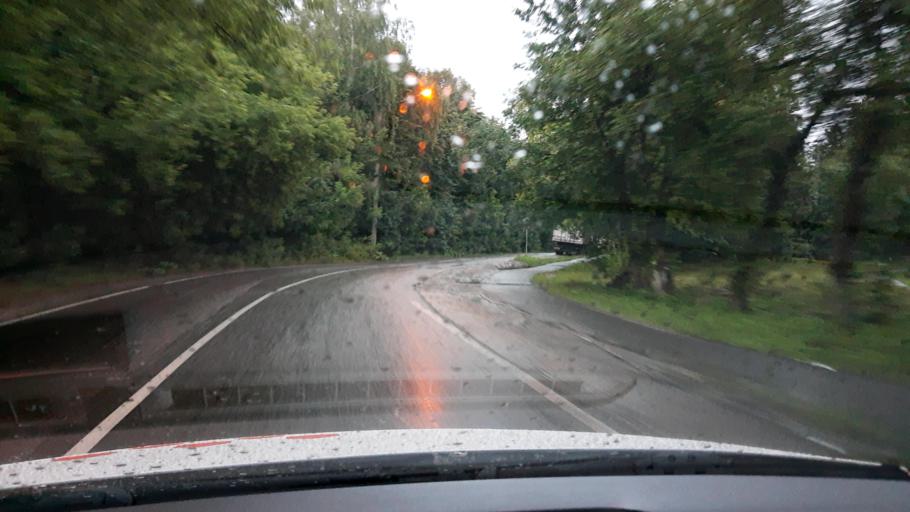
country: RU
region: Moskovskaya
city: Biryulevo Zapadnoye
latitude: 55.5687
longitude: 37.6347
